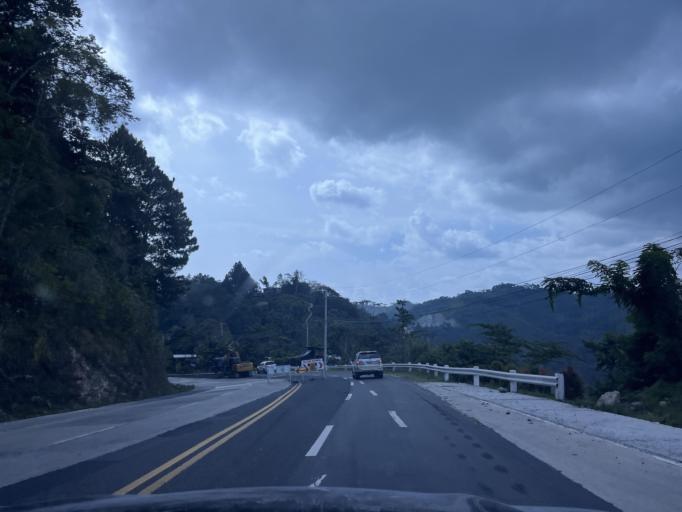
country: PH
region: Davao
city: Simod
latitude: 7.3816
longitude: 125.2789
